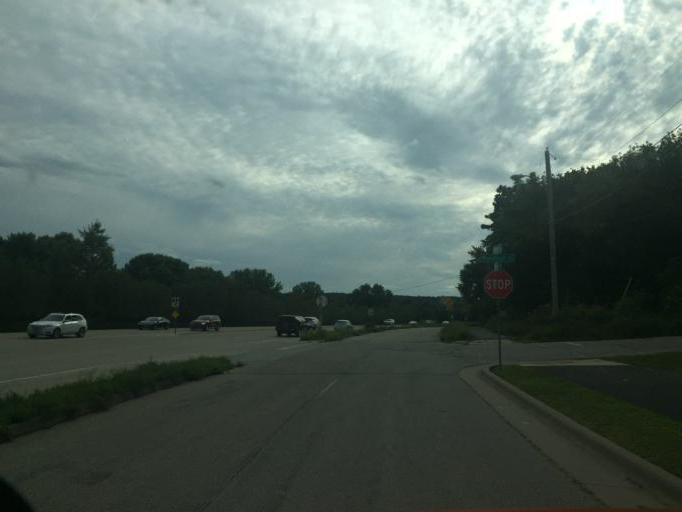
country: US
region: Minnesota
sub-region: Olmsted County
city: Rochester
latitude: 43.9998
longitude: -92.4930
